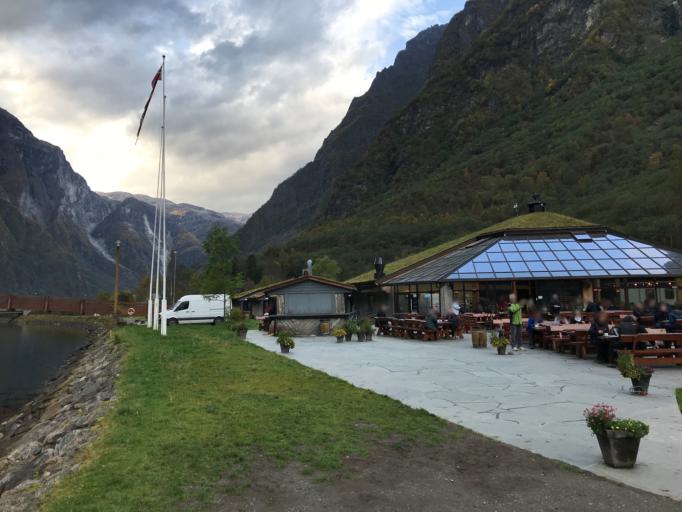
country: NO
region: Sogn og Fjordane
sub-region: Leikanger
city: Hermansverk
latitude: 60.8811
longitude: 6.8425
